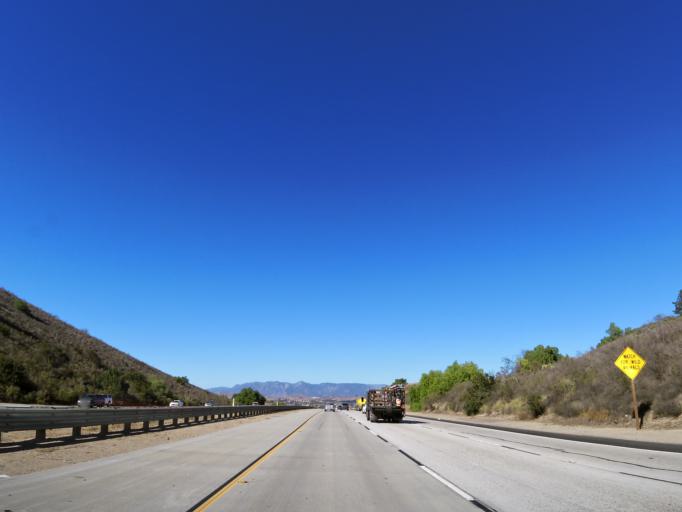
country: US
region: California
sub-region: Ventura County
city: Moorpark
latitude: 34.2708
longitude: -118.8551
